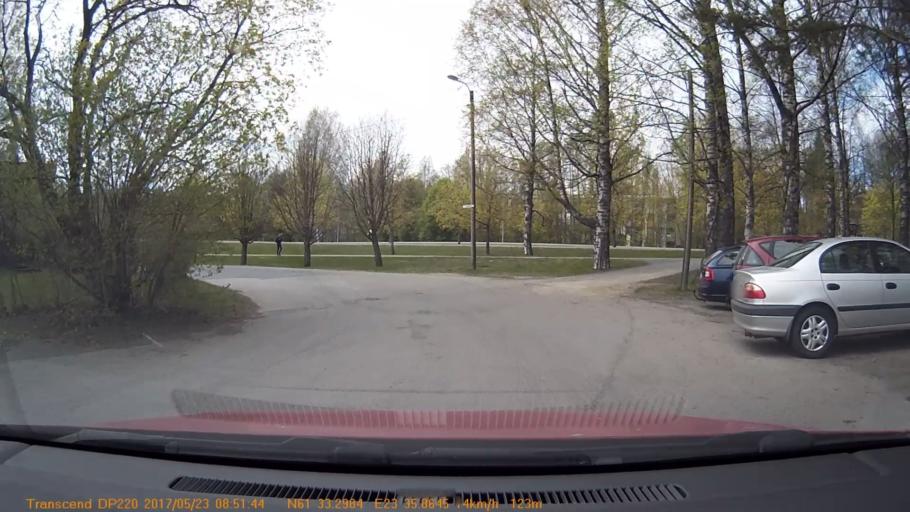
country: FI
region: Pirkanmaa
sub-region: Tampere
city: Yloejaervi
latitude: 61.5550
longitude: 23.5979
